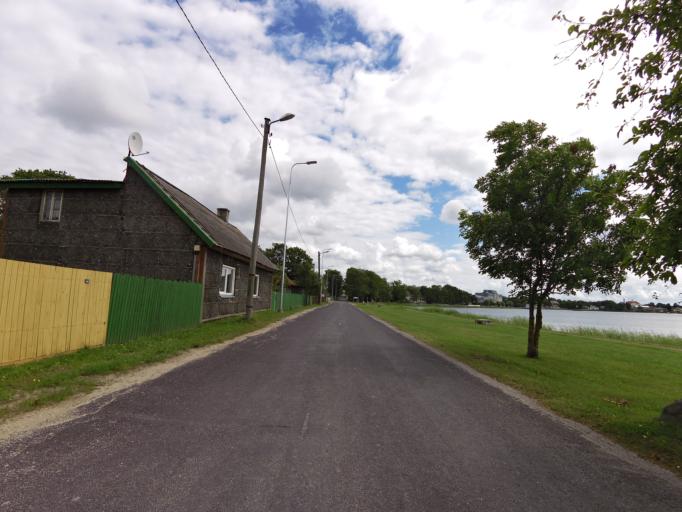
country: EE
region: Laeaene
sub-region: Haapsalu linn
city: Haapsalu
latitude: 58.9550
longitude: 23.5256
